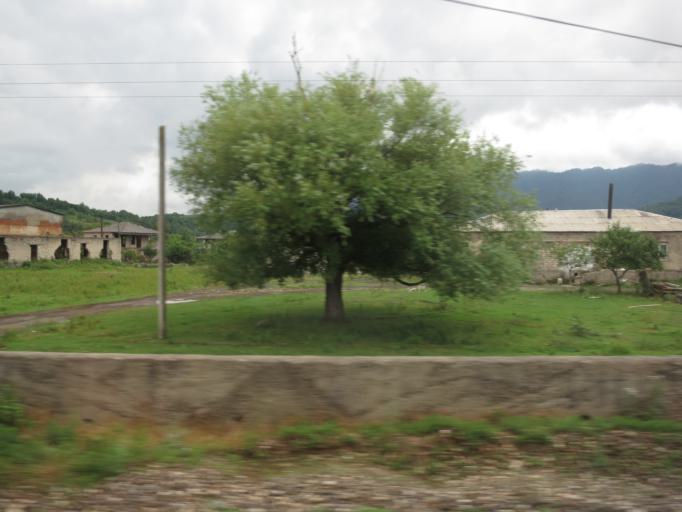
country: GE
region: Imereti
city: Samtredia
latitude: 42.0972
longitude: 42.2472
